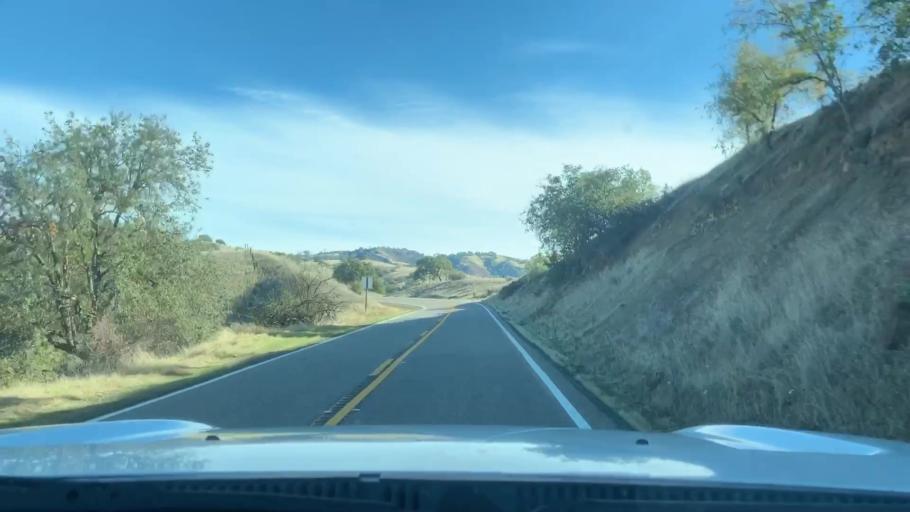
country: US
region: California
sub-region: Monterey County
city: King City
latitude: 36.1887
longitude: -120.8130
